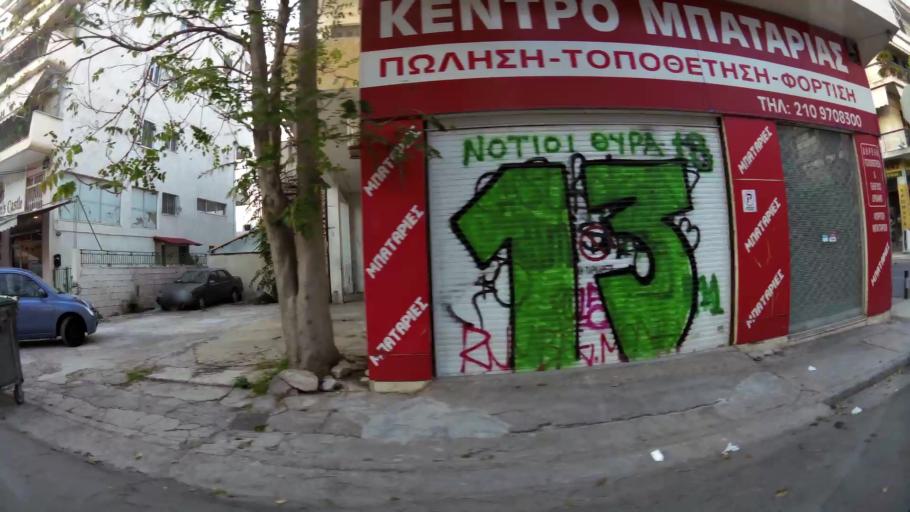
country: GR
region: Attica
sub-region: Nomarchia Athinas
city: Dhafni
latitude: 37.9477
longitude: 23.7386
